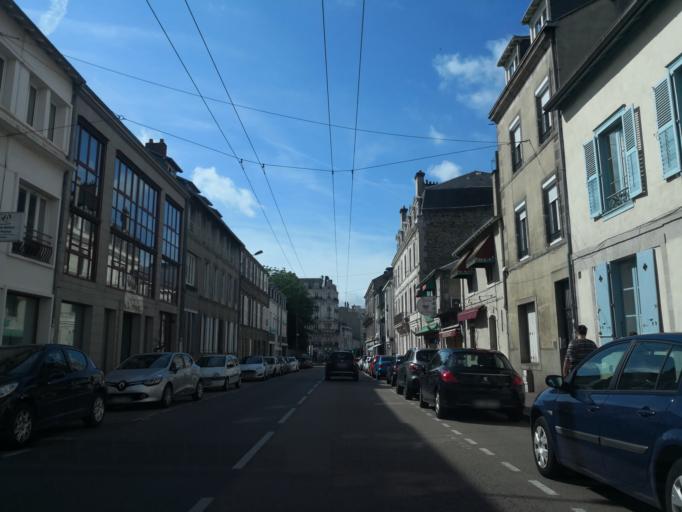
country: FR
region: Limousin
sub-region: Departement de la Haute-Vienne
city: Limoges
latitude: 45.8333
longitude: 1.2616
